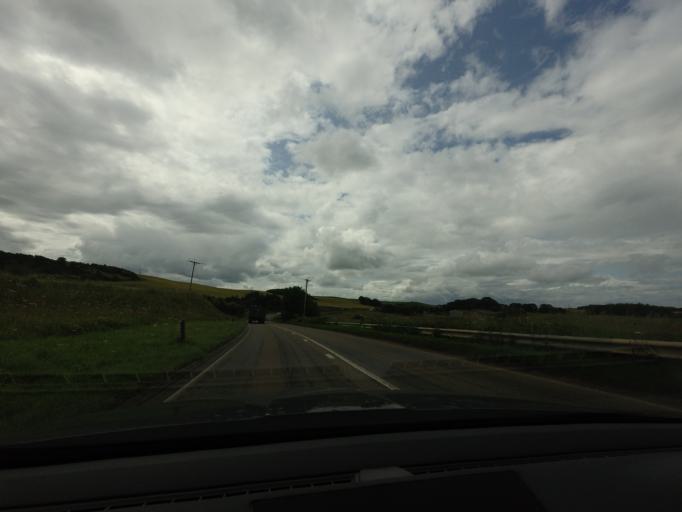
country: GB
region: Scotland
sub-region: Aberdeenshire
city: Whitehills
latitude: 57.6654
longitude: -2.5584
